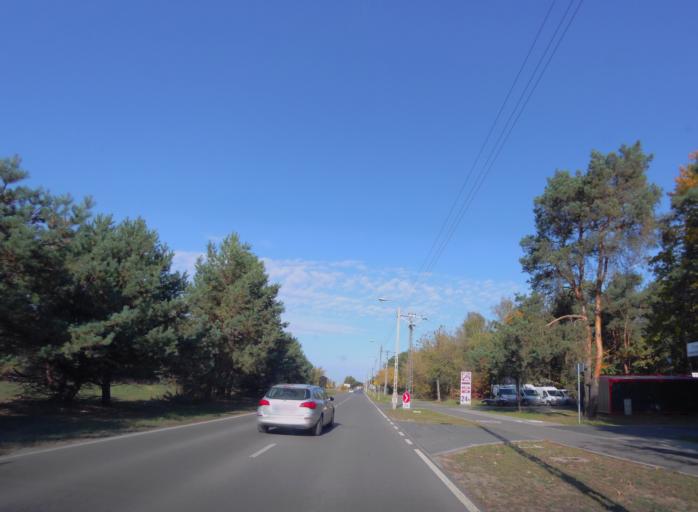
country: PL
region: Masovian Voivodeship
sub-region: Powiat otwocki
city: Jozefow
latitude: 52.1526
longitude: 21.2207
